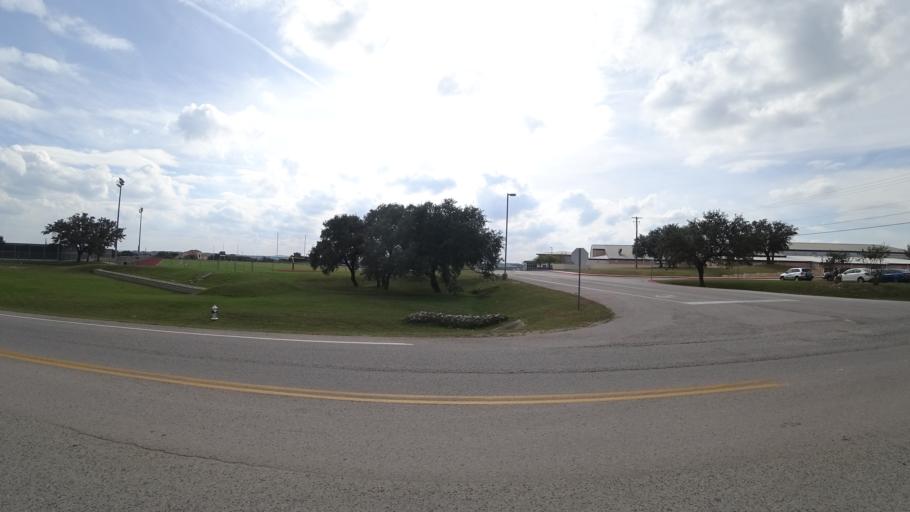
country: US
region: Texas
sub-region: Travis County
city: Hudson Bend
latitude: 30.3913
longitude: -97.9333
